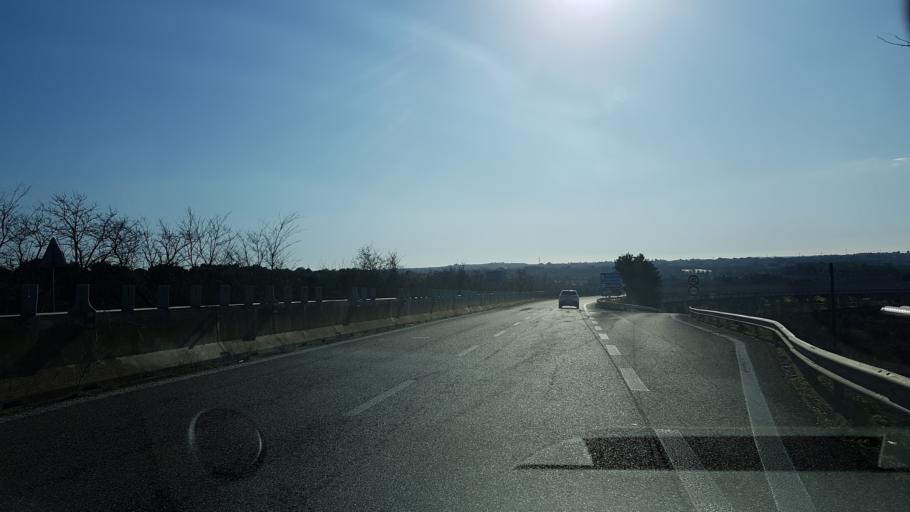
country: IT
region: Apulia
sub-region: Provincia di Lecce
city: Sannicola
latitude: 40.0942
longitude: 18.0306
